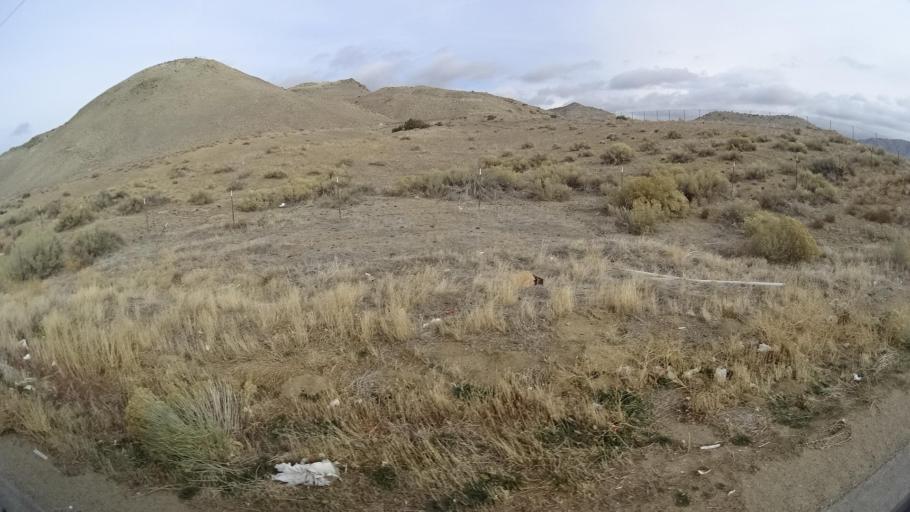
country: US
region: California
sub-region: Kern County
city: Tehachapi
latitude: 35.1207
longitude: -118.3455
